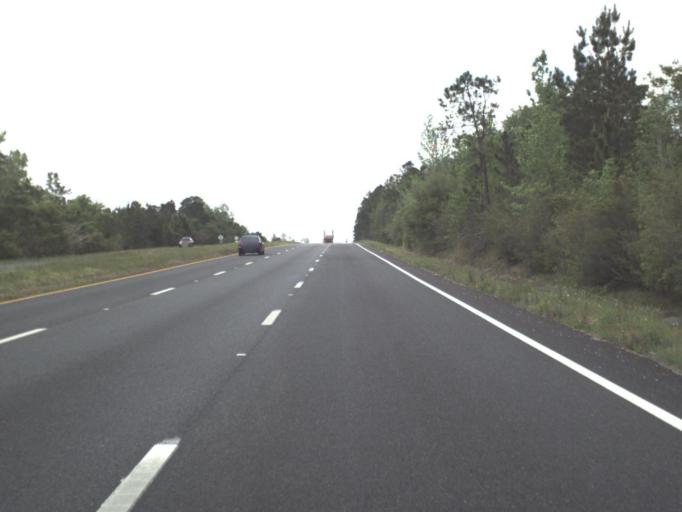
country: US
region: Florida
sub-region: Escambia County
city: Molino
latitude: 30.7979
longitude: -87.3345
